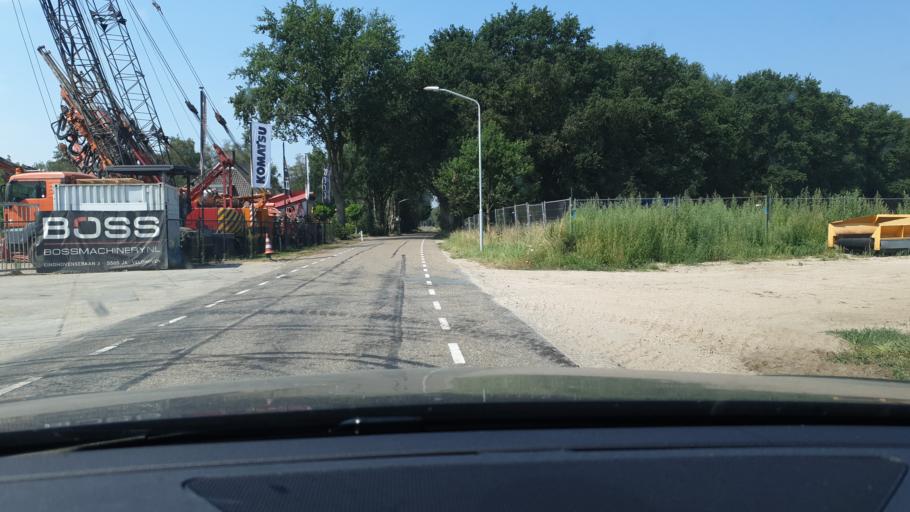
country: NL
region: North Brabant
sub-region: Gemeente Veldhoven
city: Oerle
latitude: 51.4129
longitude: 5.3796
